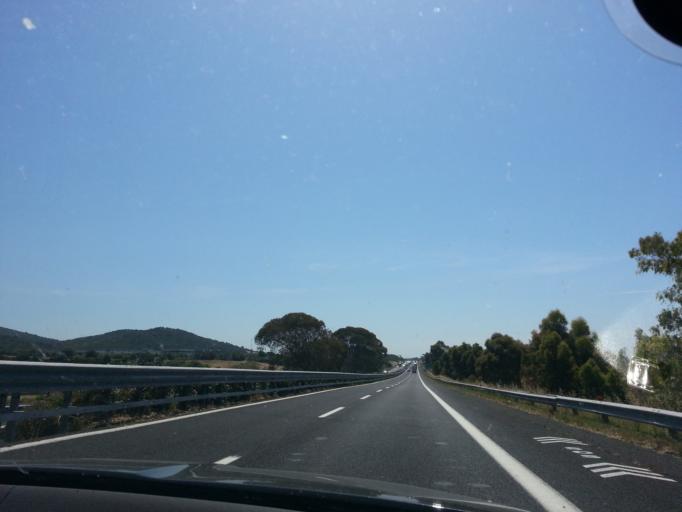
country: IT
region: Latium
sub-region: Citta metropolitana di Roma Capitale
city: Santa Marinella
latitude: 42.0429
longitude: 11.9275
